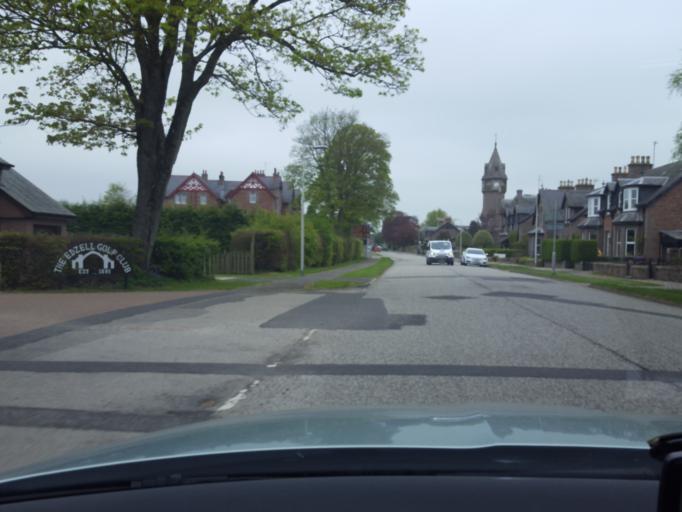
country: GB
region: Scotland
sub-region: Angus
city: Brechin
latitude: 56.8058
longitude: -2.6535
